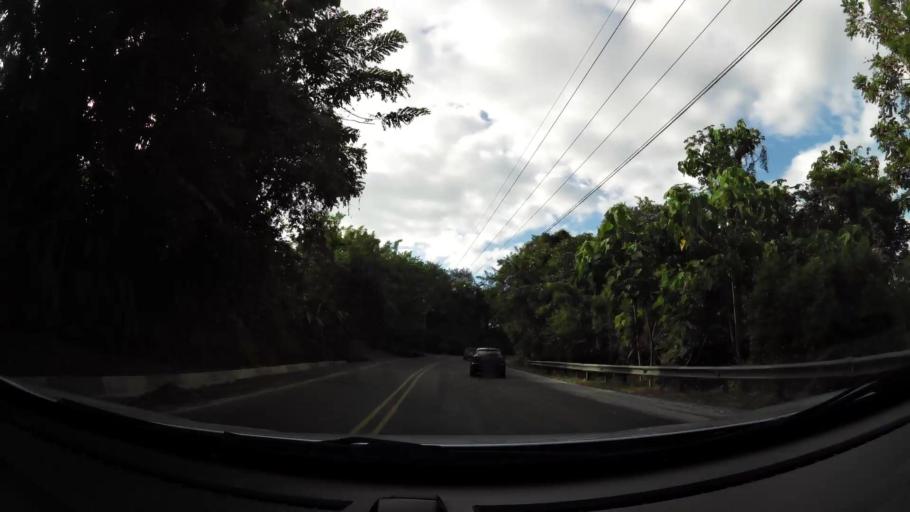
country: CR
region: Puntarenas
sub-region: Canton de Garabito
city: Jaco
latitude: 9.6717
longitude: -84.6401
